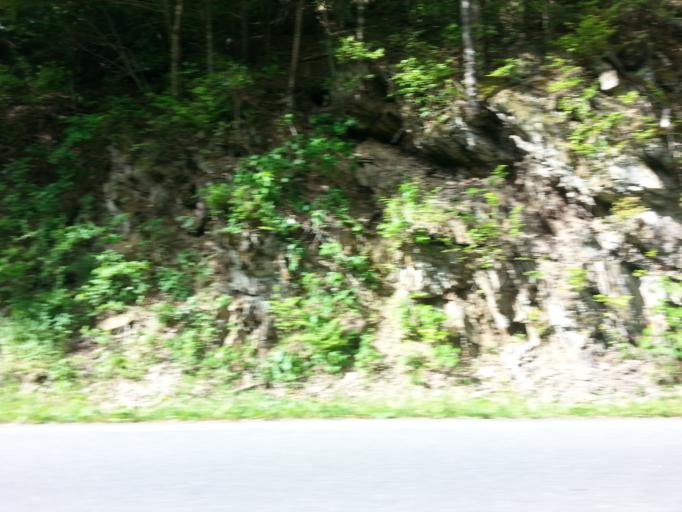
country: US
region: Tennessee
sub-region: Sevier County
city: Gatlinburg
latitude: 35.6095
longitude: -83.4363
